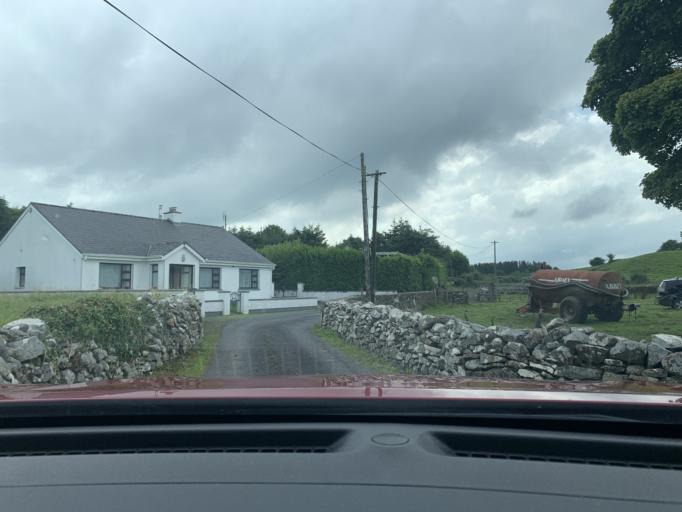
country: IE
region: Connaught
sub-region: Maigh Eo
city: Kiltamagh
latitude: 53.8425
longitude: -9.0072
